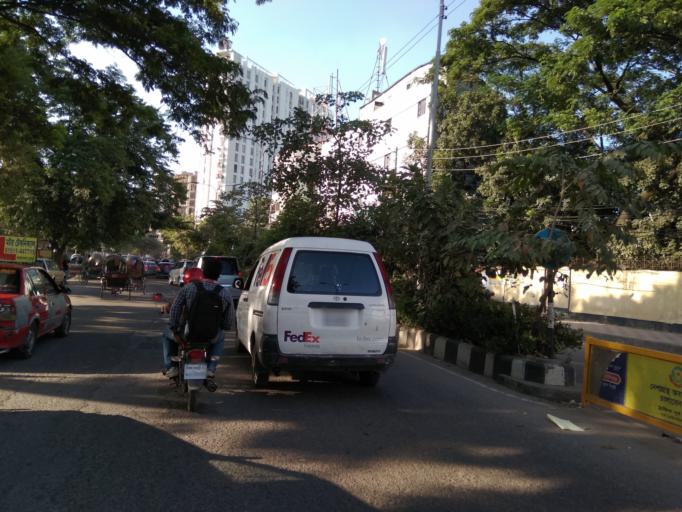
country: BD
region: Dhaka
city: Paltan
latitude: 23.7392
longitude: 90.4208
